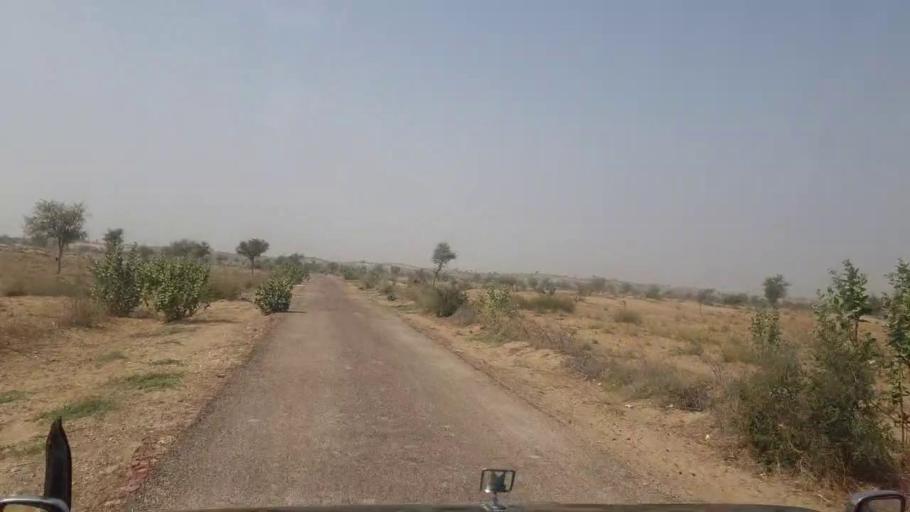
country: PK
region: Sindh
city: Islamkot
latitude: 25.0917
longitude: 70.1648
